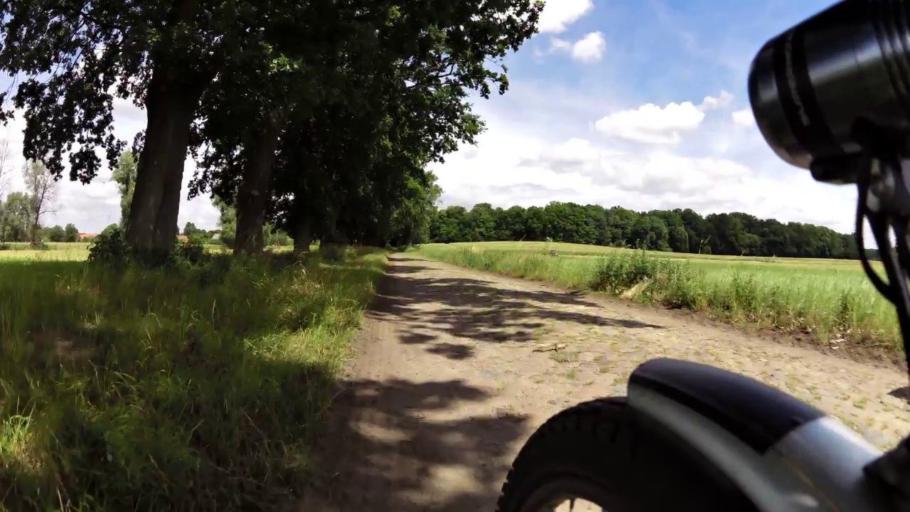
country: PL
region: West Pomeranian Voivodeship
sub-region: Powiat choszczenski
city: Choszczno
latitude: 53.2258
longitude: 15.3860
